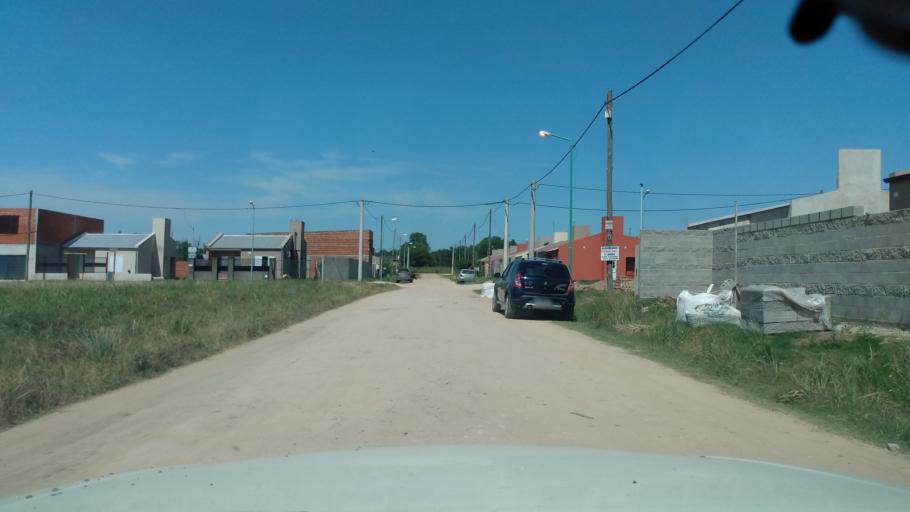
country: AR
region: Buenos Aires
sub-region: Partido de Lujan
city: Lujan
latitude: -34.5535
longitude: -59.1366
